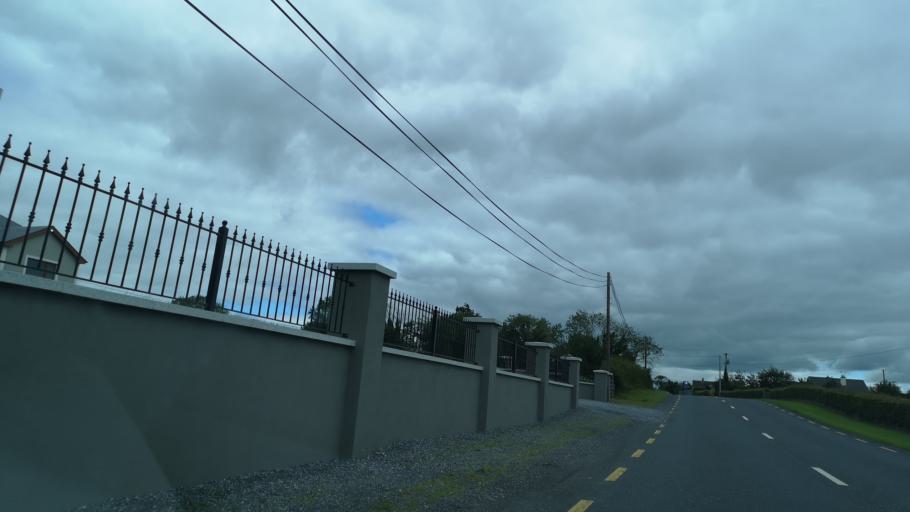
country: IE
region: Connaught
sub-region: County Galway
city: Ballinasloe
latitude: 53.3013
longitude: -8.1285
